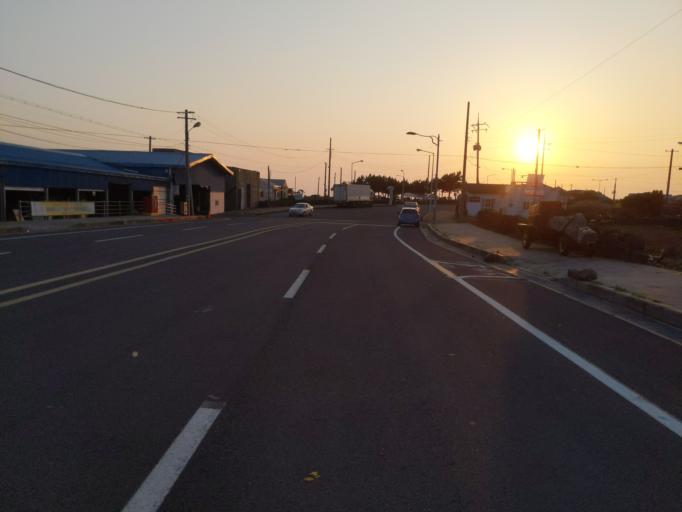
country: KR
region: Jeju-do
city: Gaigeturi
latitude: 33.2207
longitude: 126.2485
